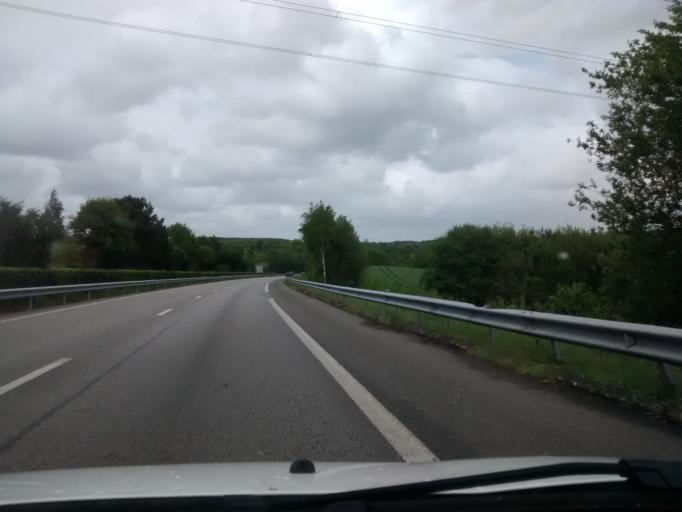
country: FR
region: Brittany
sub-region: Departement du Morbihan
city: Elven
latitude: 47.7432
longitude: -2.5744
